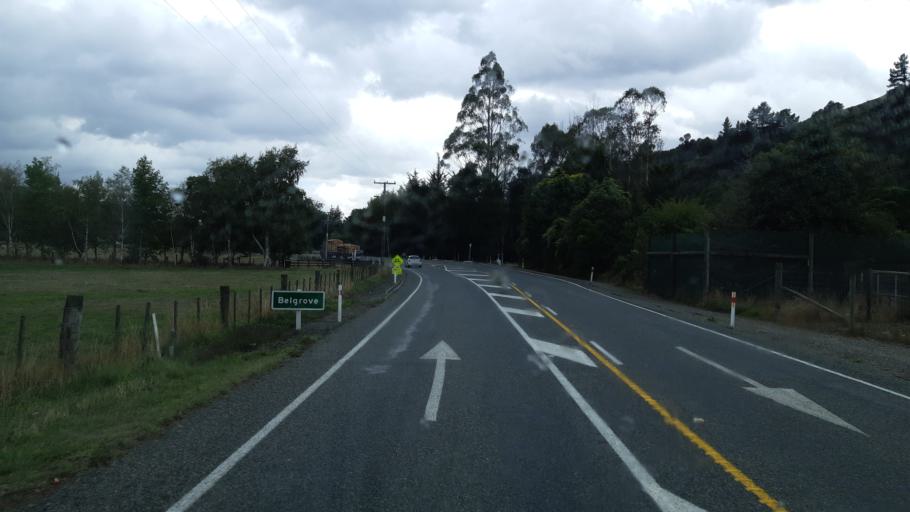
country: NZ
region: Tasman
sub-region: Tasman District
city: Wakefield
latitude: -41.4555
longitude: 172.9548
